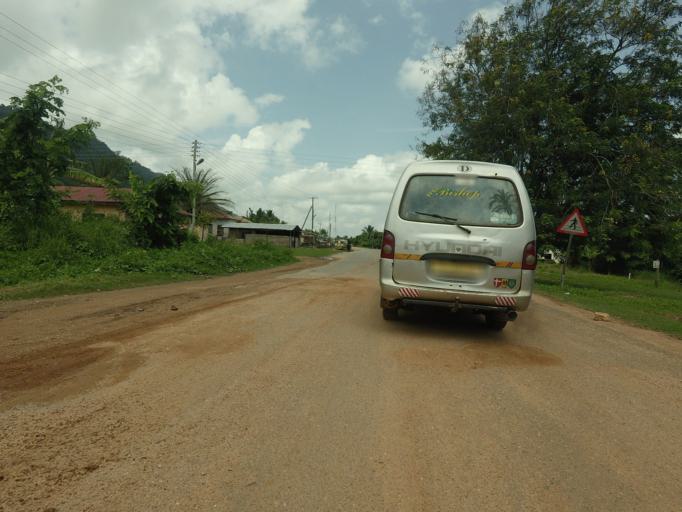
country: GH
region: Volta
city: Ho
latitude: 6.7625
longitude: 0.3634
